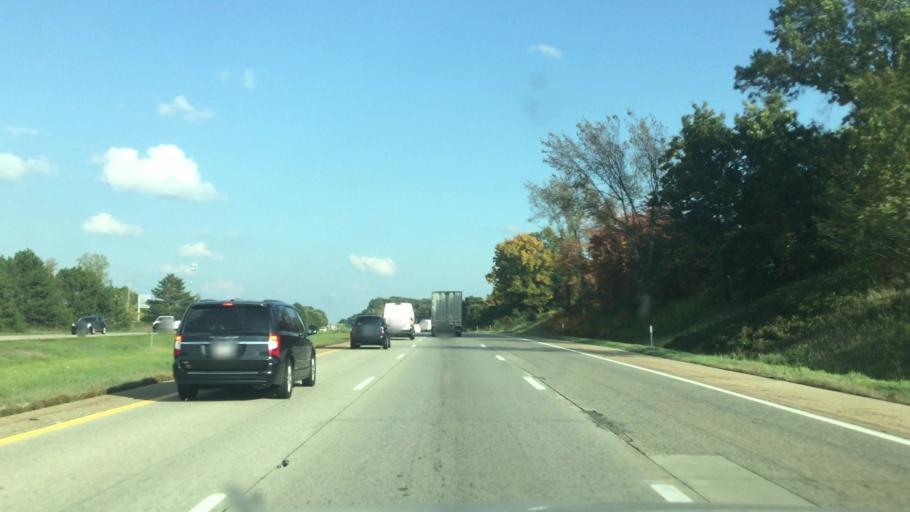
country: US
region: Michigan
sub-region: Calhoun County
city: Albion
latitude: 42.2622
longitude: -84.7027
